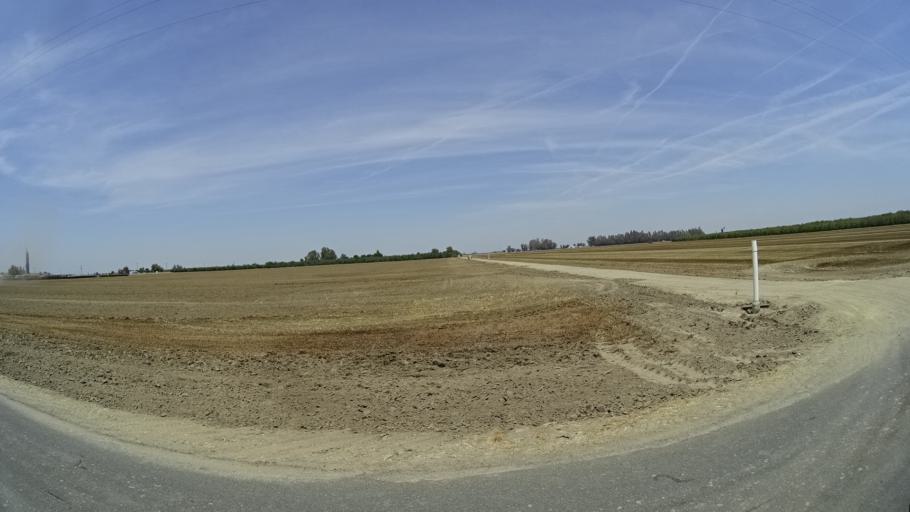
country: US
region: California
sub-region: Fresno County
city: Riverdale
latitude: 36.3947
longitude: -119.8478
